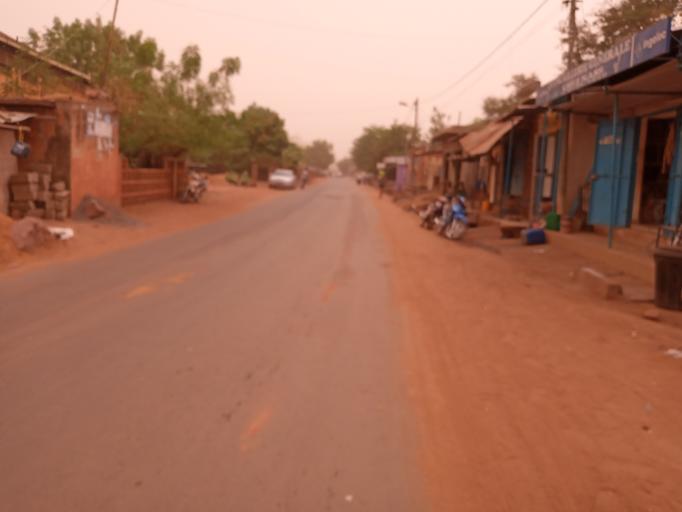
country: ML
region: Koulikoro
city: Koulikoro
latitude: 12.8610
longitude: -7.5584
